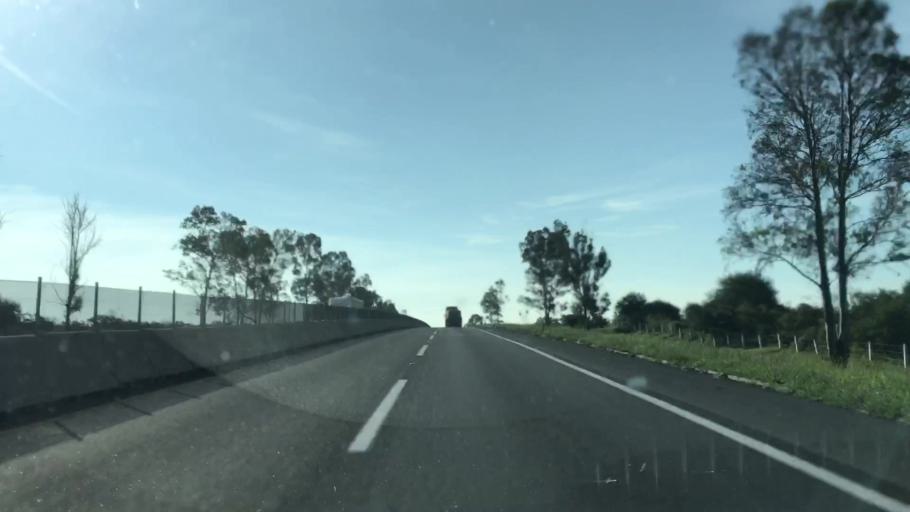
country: MX
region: Jalisco
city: Encarnacion de Diaz
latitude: 21.4685
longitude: -102.2202
